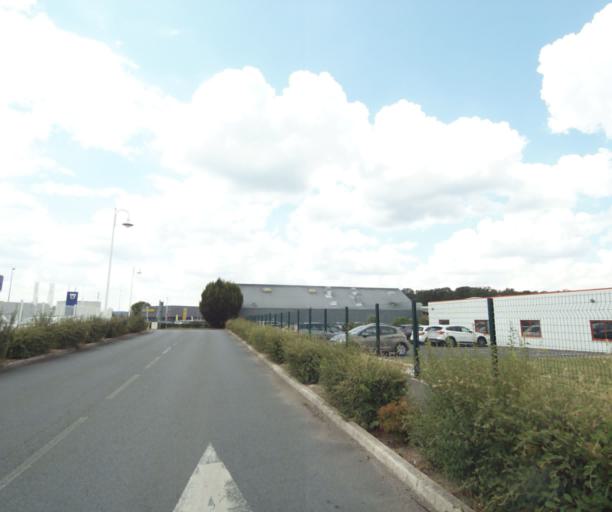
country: FR
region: Ile-de-France
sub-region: Departement de Seine-et-Marne
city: Vulaines-sur-Seine
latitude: 48.4235
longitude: 2.7707
